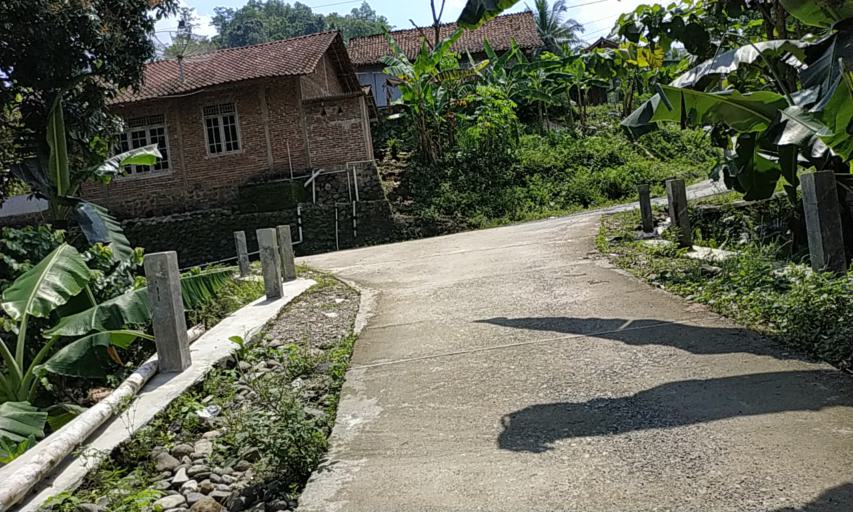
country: ID
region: Central Java
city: Kutoarjo
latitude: -7.6221
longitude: 109.7290
